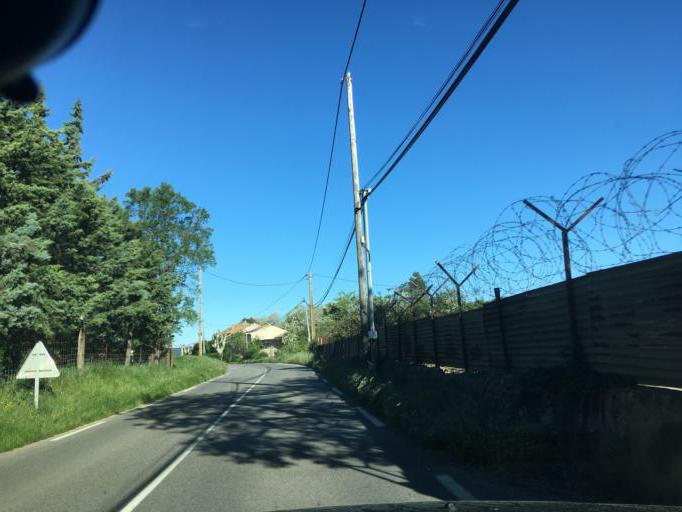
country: FR
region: Provence-Alpes-Cote d'Azur
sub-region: Departement du Var
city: Rians
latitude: 43.6136
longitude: 5.7467
